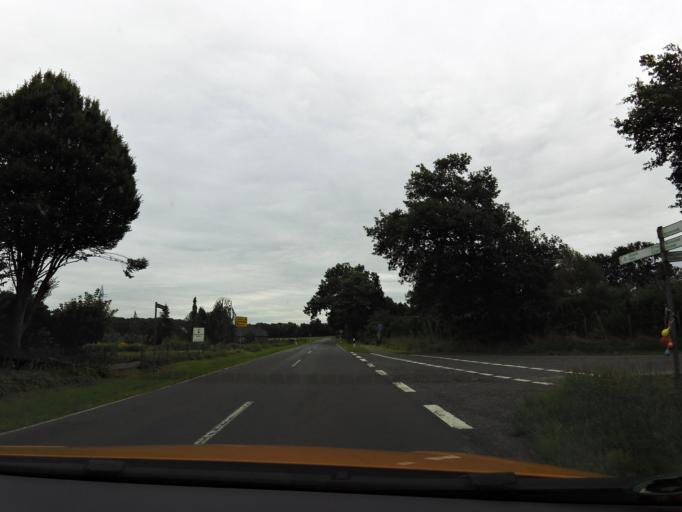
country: DE
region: Lower Saxony
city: Wiefelstede
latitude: 53.2110
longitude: 8.0791
